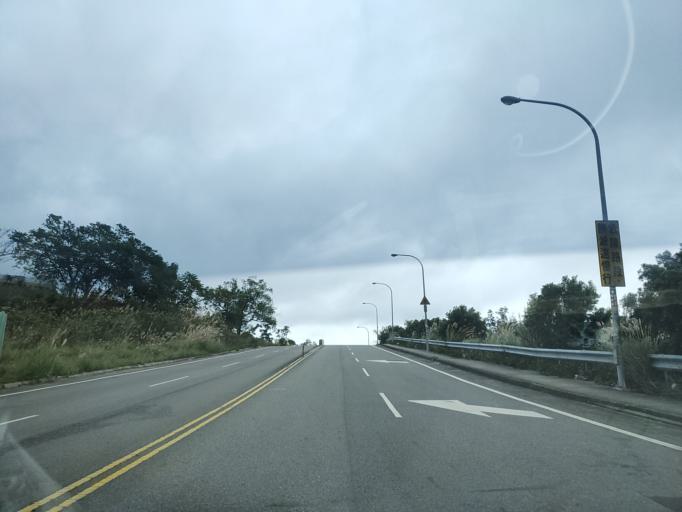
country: TW
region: Taiwan
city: Fengyuan
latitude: 24.3870
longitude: 120.7583
